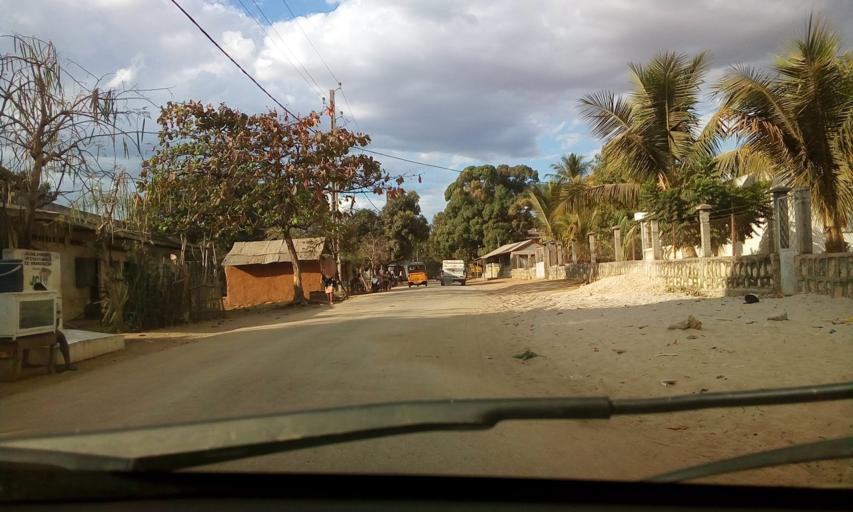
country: MG
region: Boeny
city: Mahajanga
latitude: -15.7080
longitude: 46.3311
